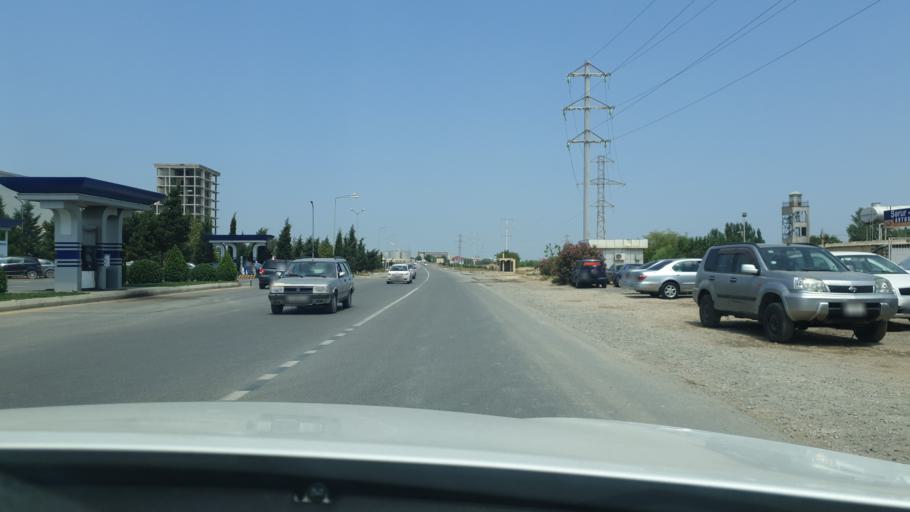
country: AZ
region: Baki
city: Qaracuxur
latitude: 40.3992
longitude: 50.0003
